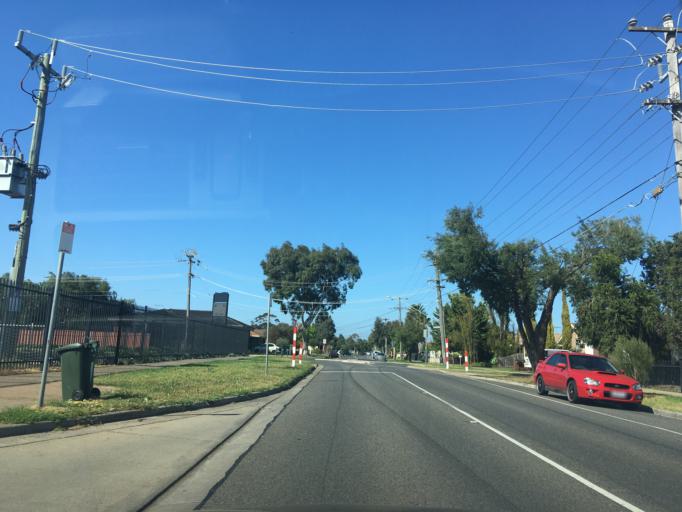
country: AU
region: Victoria
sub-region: Wyndham
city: Hoppers Crossing
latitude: -37.8705
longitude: 144.7101
